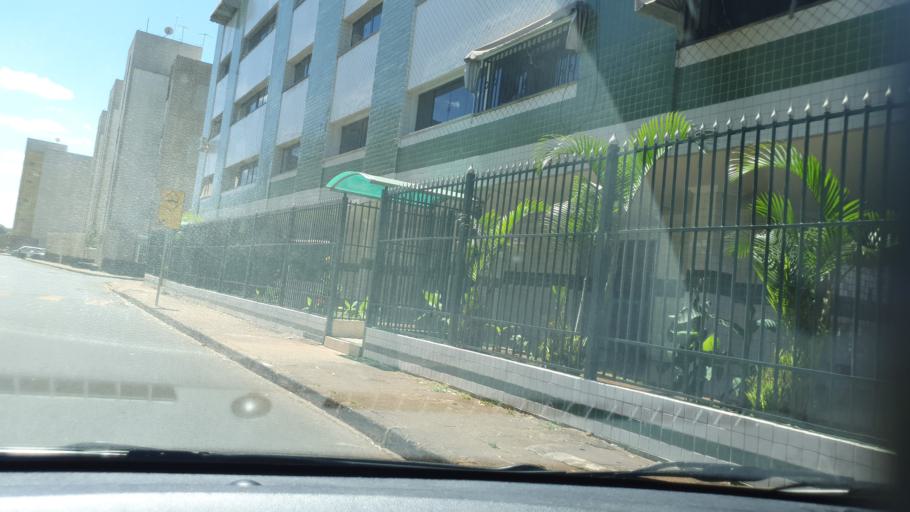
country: BR
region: Federal District
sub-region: Brasilia
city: Brasilia
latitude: -15.7940
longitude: -47.9376
